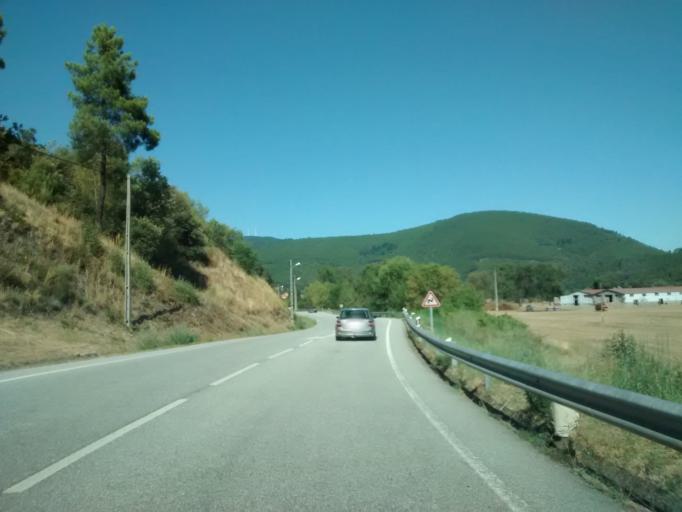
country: PT
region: Castelo Branco
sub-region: Belmonte
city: Belmonte
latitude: 40.3993
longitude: -7.4177
